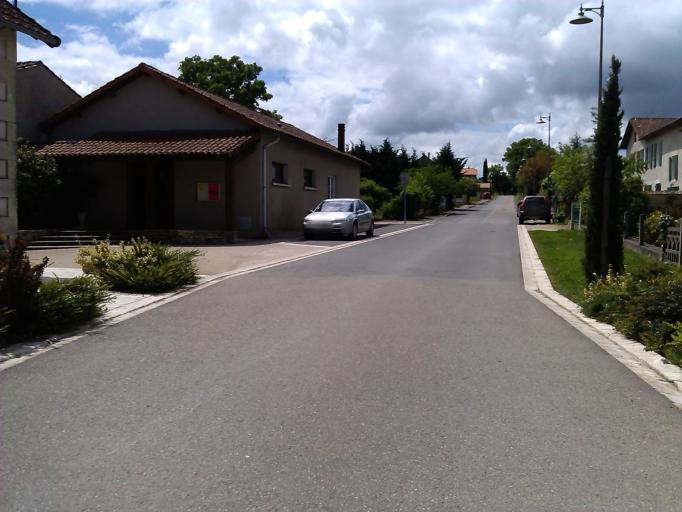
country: FR
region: Poitou-Charentes
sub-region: Departement de la Charente
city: Champagne-Mouton
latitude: 46.0365
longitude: 0.4511
